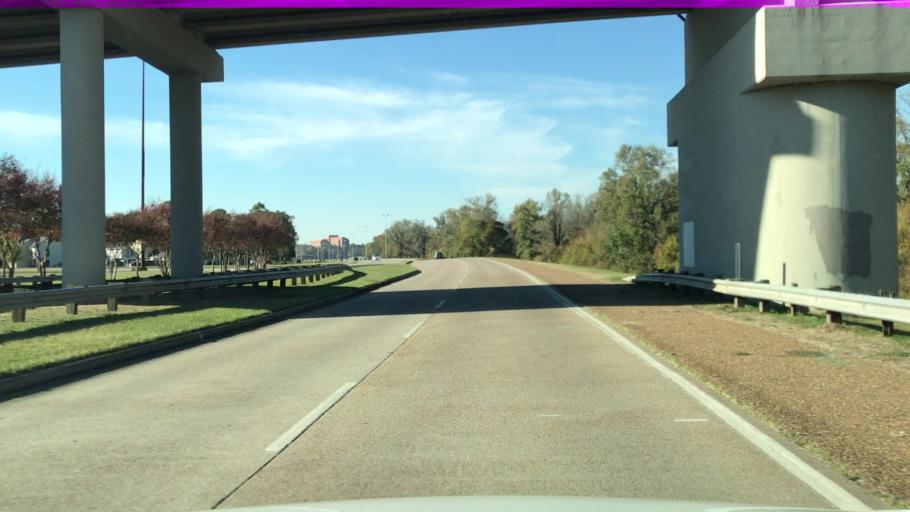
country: US
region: Louisiana
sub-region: Bossier Parish
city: Bossier City
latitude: 32.4910
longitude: -93.7009
